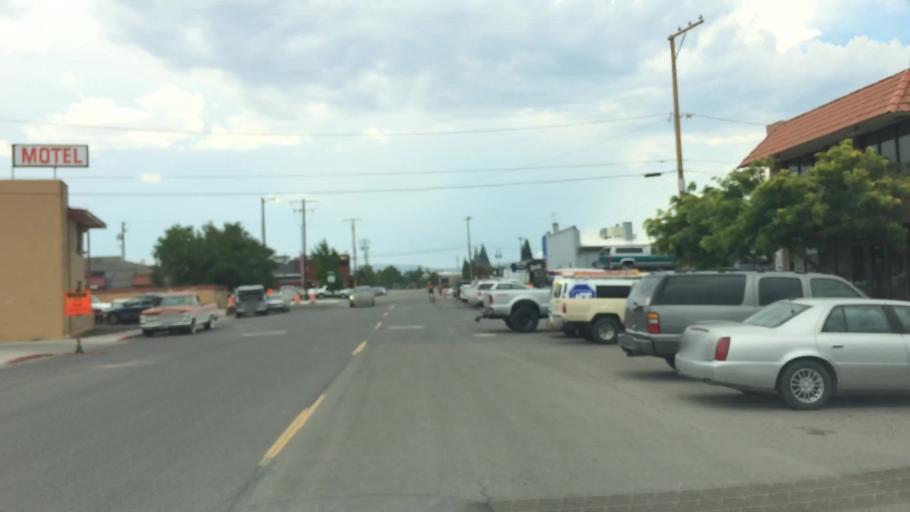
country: US
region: Nevada
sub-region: Washoe County
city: Reno
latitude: 39.5333
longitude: -119.8007
